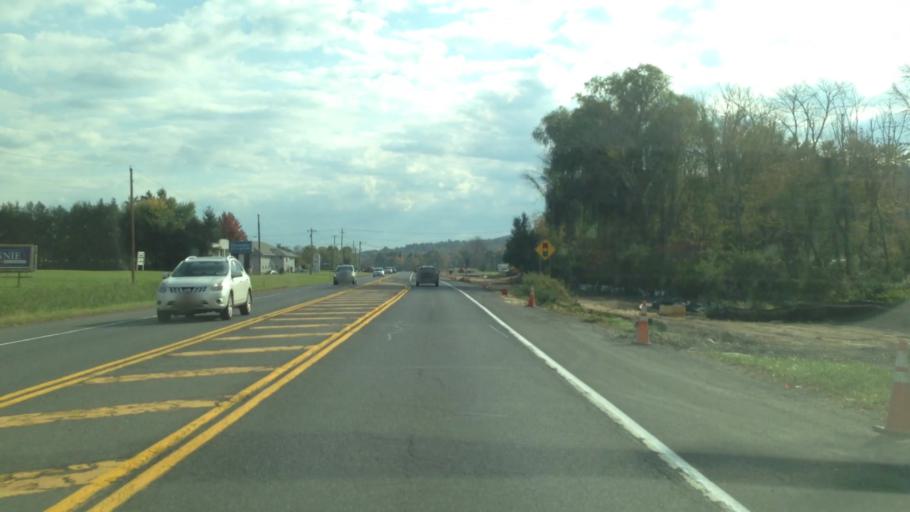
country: US
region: New York
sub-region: Ulster County
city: Clintondale
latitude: 41.7384
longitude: -74.0405
